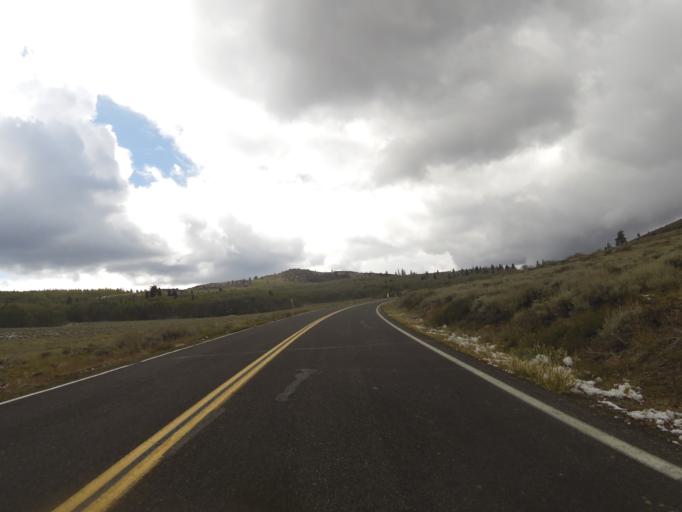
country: US
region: Nevada
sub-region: Douglas County
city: Gardnerville Ranchos
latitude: 38.6745
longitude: -119.6037
